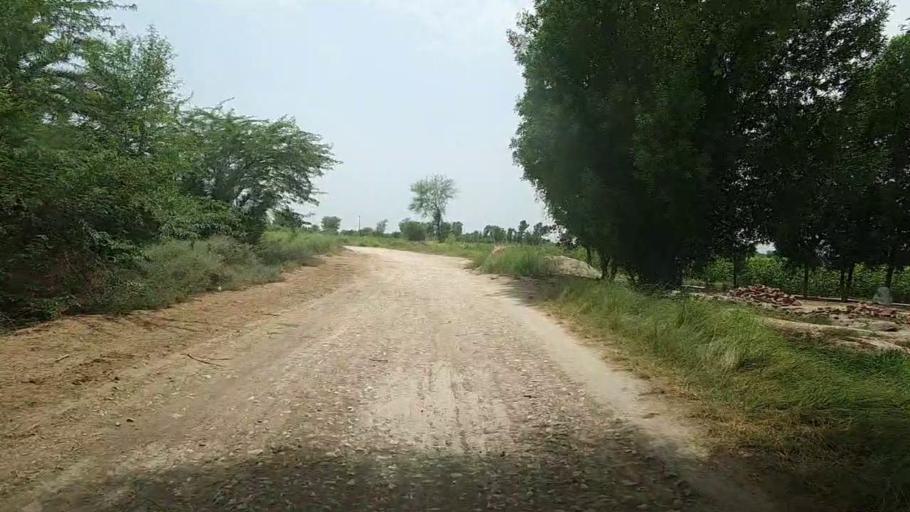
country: PK
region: Sindh
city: Karaundi
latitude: 26.9080
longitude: 68.3213
